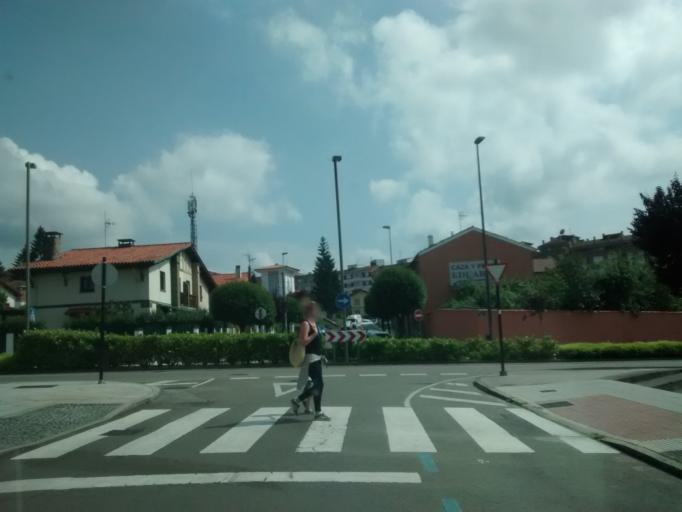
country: ES
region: Asturias
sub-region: Province of Asturias
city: Pola de Siero
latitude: 43.3921
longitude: -5.6587
